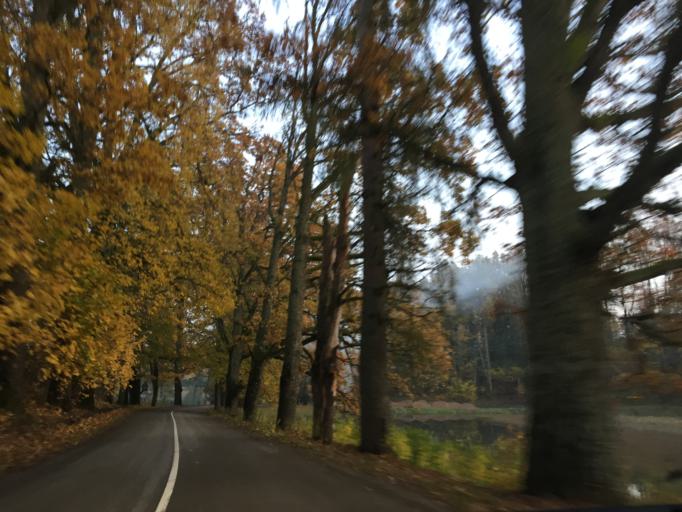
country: LV
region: Cesu Rajons
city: Cesis
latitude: 57.3093
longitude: 25.1636
